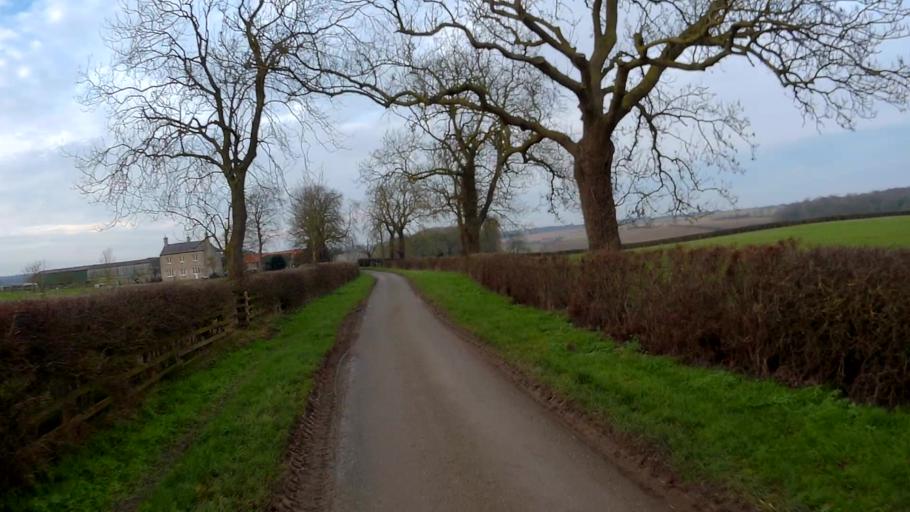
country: GB
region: England
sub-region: Lincolnshire
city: Bourne
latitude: 52.8230
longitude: -0.4582
